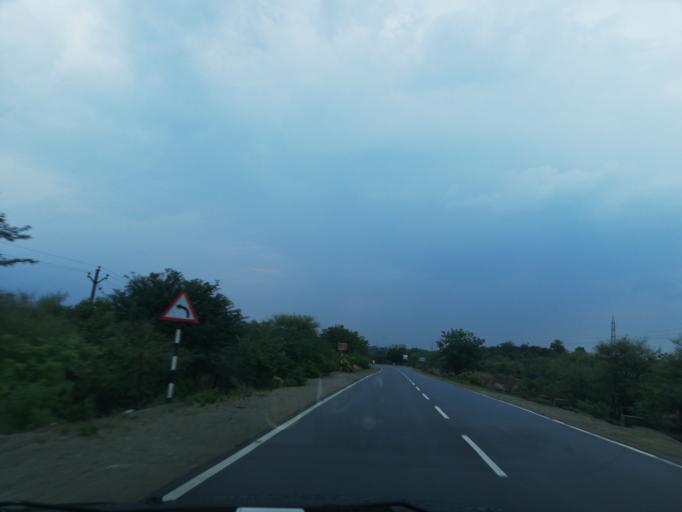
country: IN
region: Andhra Pradesh
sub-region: Guntur
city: Macherla
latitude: 16.6640
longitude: 79.2858
